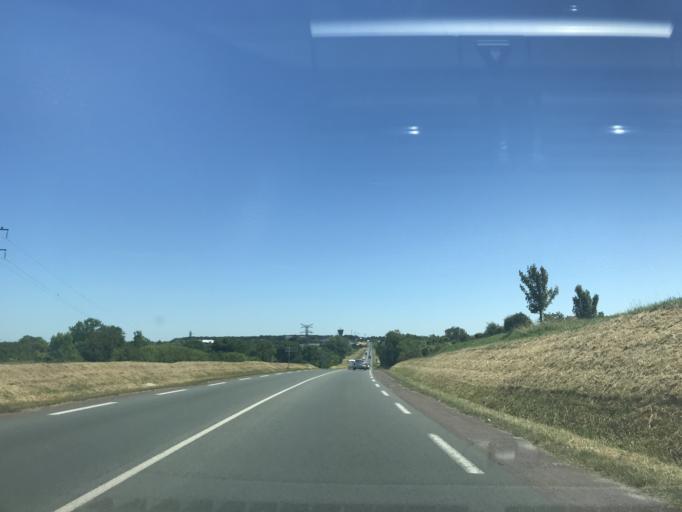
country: FR
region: Poitou-Charentes
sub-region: Departement de la Charente-Maritime
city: Royan
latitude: 45.6379
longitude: -1.0199
